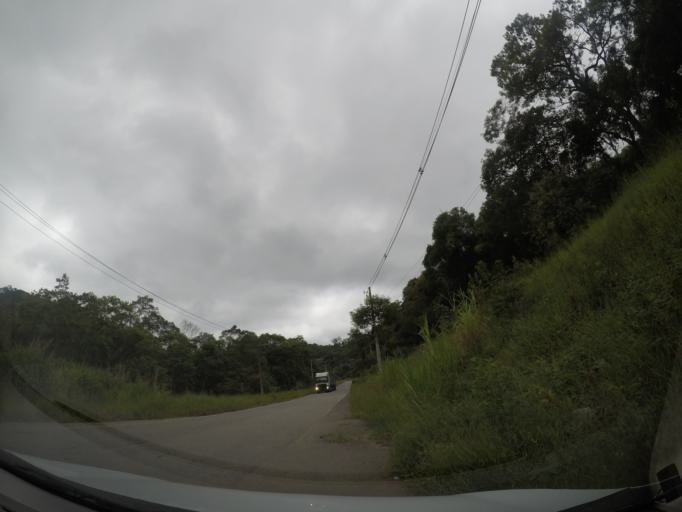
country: BR
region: Sao Paulo
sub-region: Aruja
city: Aruja
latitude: -23.3525
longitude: -46.4066
